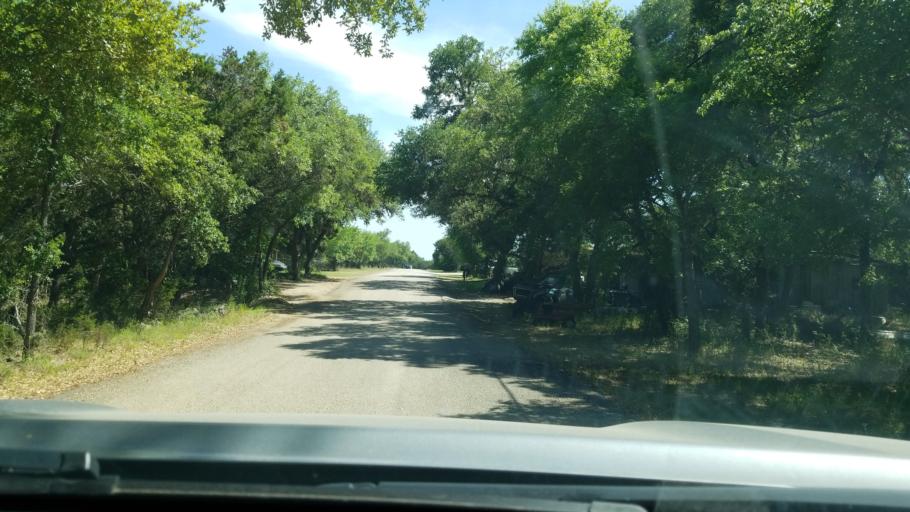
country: US
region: Texas
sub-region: Bexar County
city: Timberwood Park
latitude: 29.7495
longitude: -98.5179
